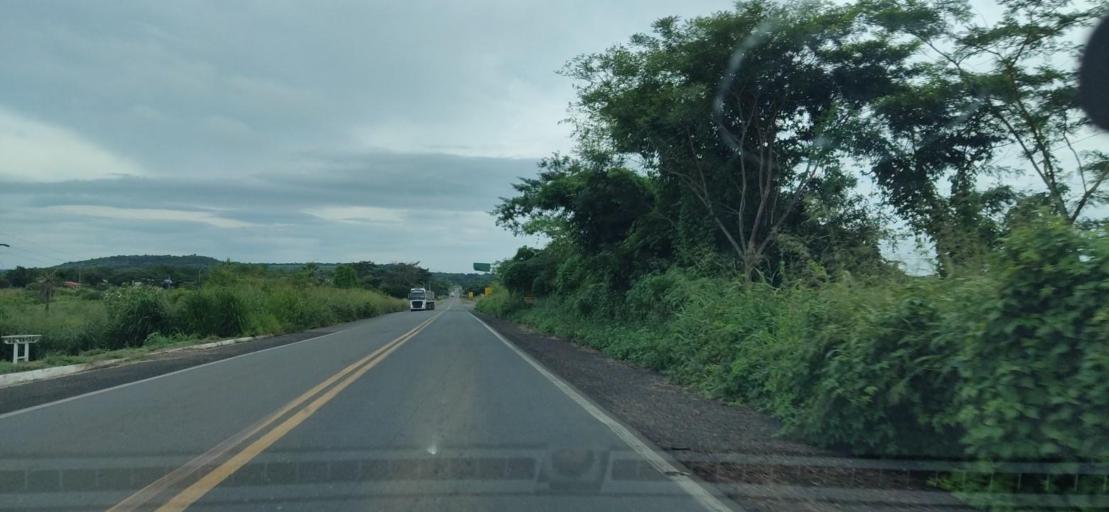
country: BR
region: Piaui
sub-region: Elesbao Veloso
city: Elesbao Veloso
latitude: -6.1906
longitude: -42.1191
